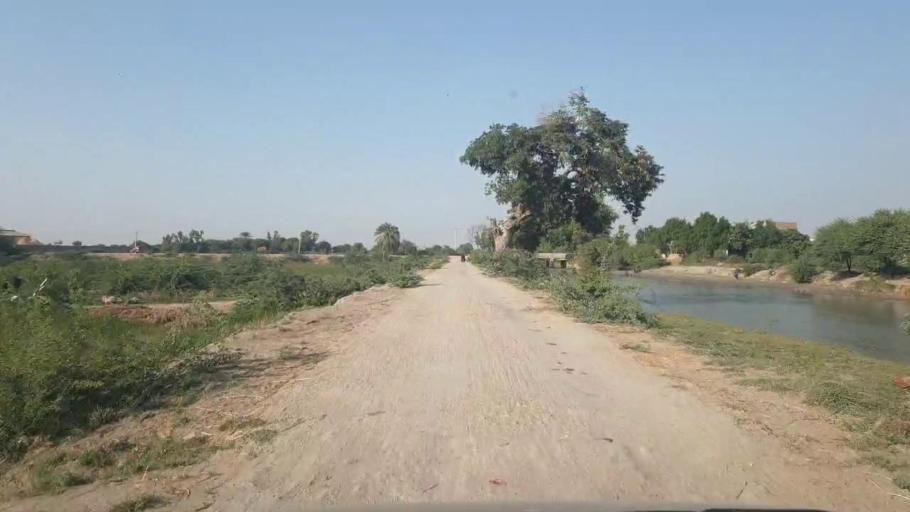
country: PK
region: Sindh
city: Badin
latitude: 24.6533
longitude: 68.8152
